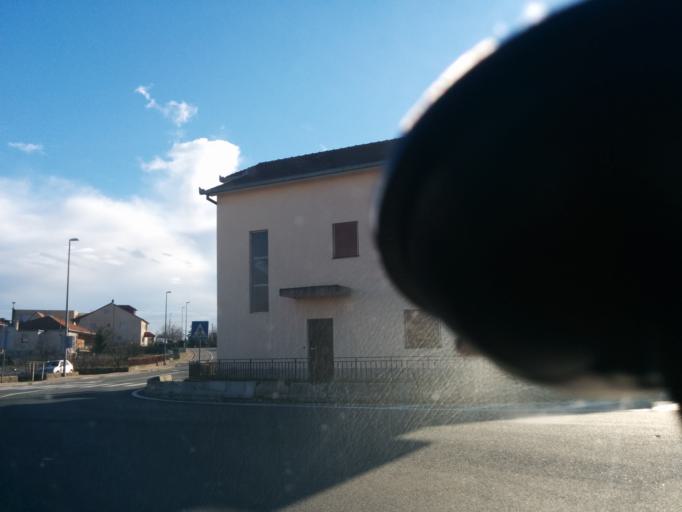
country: HR
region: Splitsko-Dalmatinska
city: Brnaze
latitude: 43.6805
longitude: 16.6498
